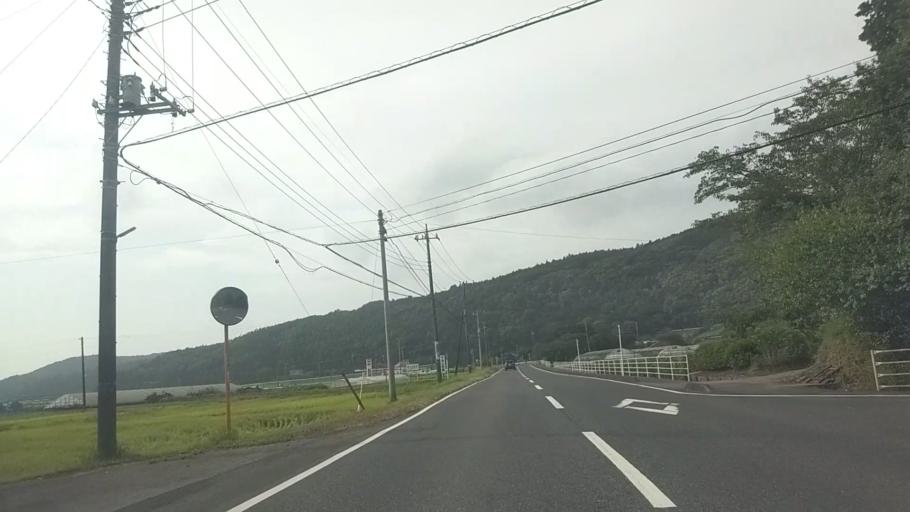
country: JP
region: Chiba
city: Kisarazu
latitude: 35.3063
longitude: 139.9776
